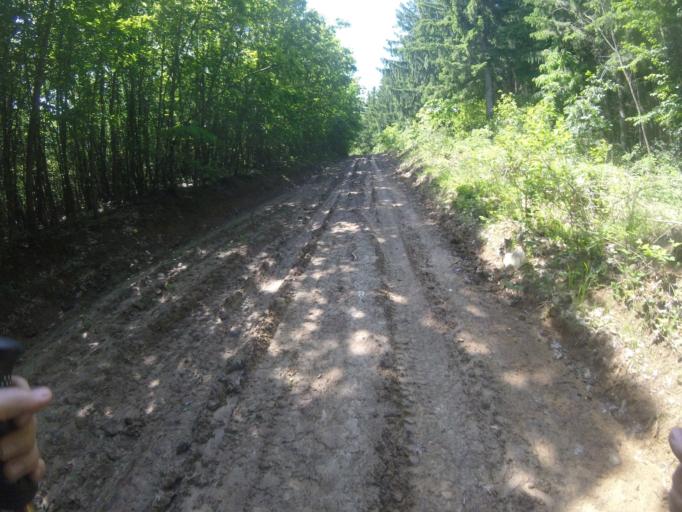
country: HU
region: Nograd
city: Matraverebely
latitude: 47.9384
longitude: 19.7946
